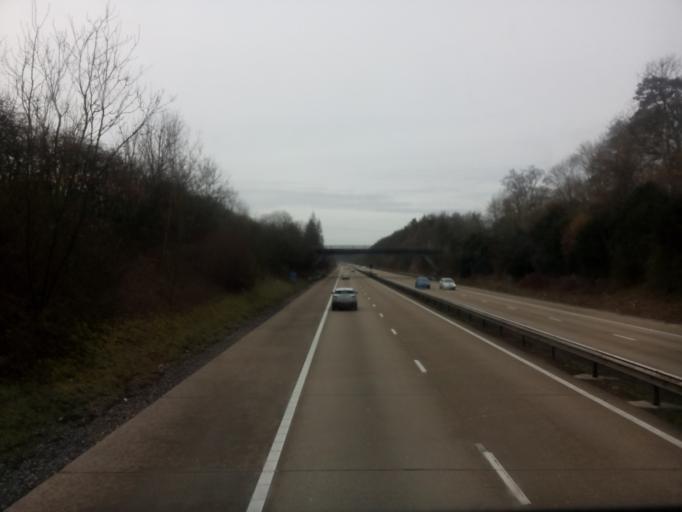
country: GB
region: England
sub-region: Hampshire
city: Overton
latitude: 51.1784
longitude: -1.2184
